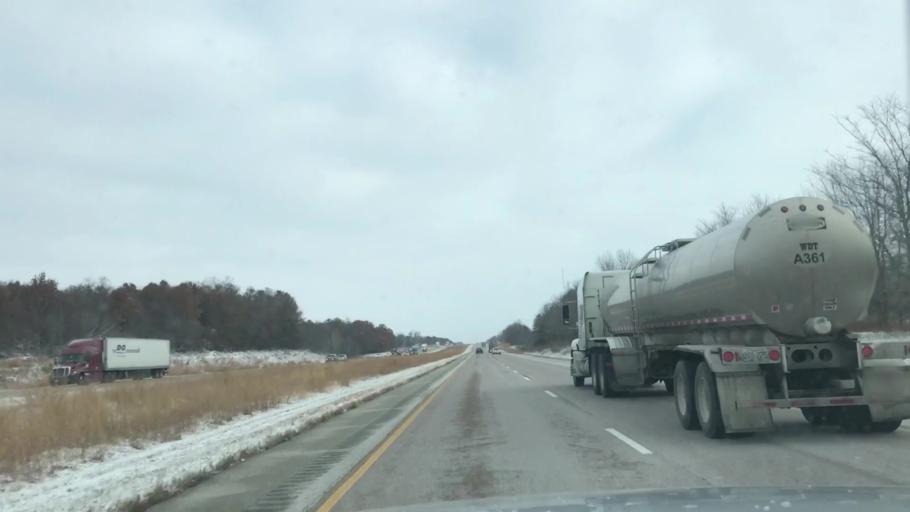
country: US
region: Illinois
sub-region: Macoupin County
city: Mount Olive
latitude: 39.0996
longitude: -89.7348
